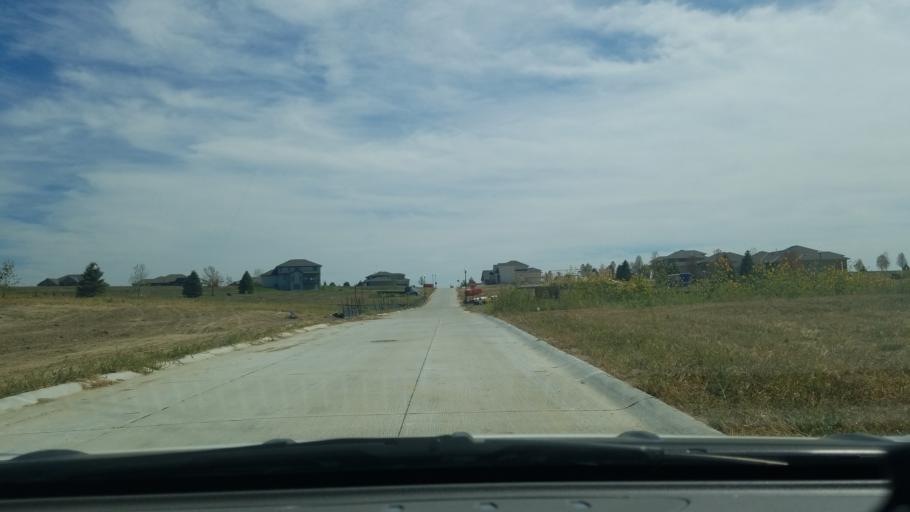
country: US
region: Nebraska
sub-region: Sarpy County
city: Chalco
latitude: 41.1413
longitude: -96.1082
